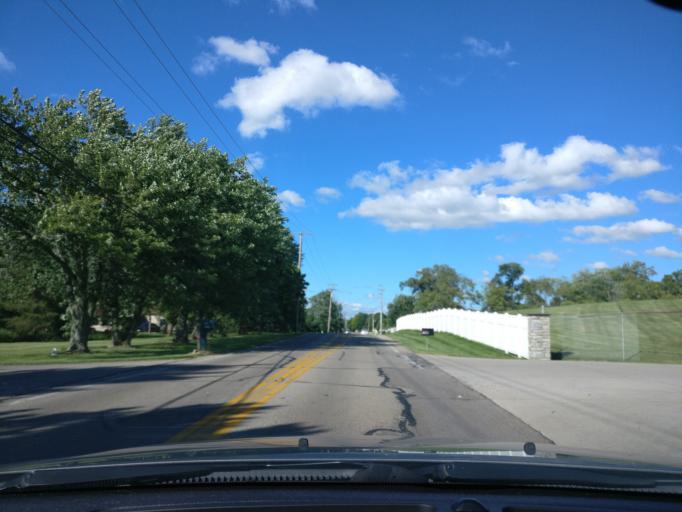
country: US
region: Ohio
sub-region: Warren County
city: Five Points
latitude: 39.5949
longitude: -84.1780
